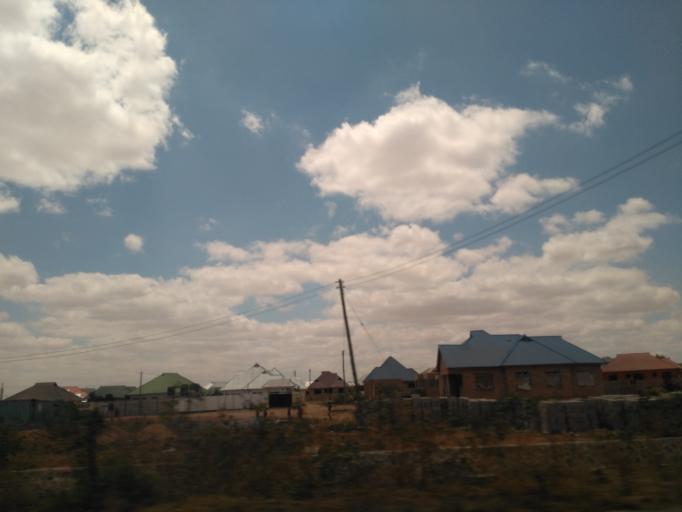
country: TZ
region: Dodoma
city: Kisasa
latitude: -6.1783
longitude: 35.7936
